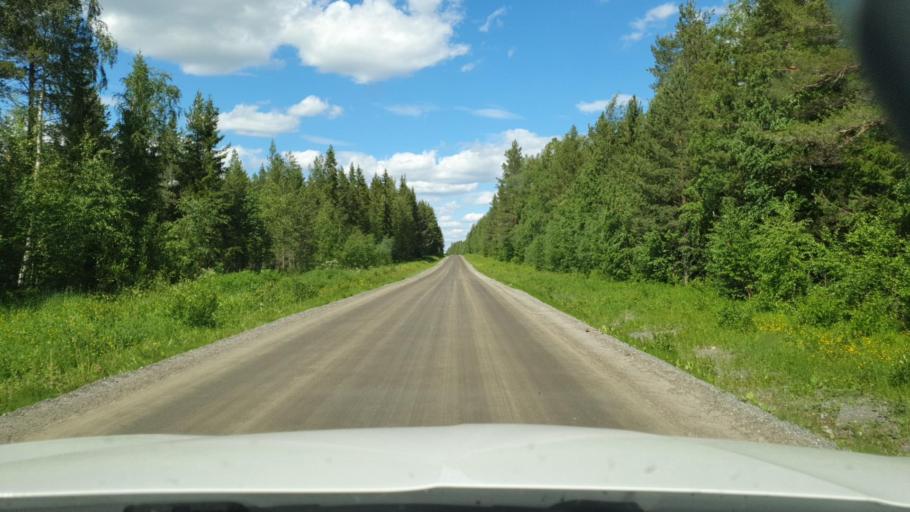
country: SE
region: Vaesterbotten
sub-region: Skelleftea Kommun
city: Forsbacka
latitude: 64.7705
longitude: 20.5173
